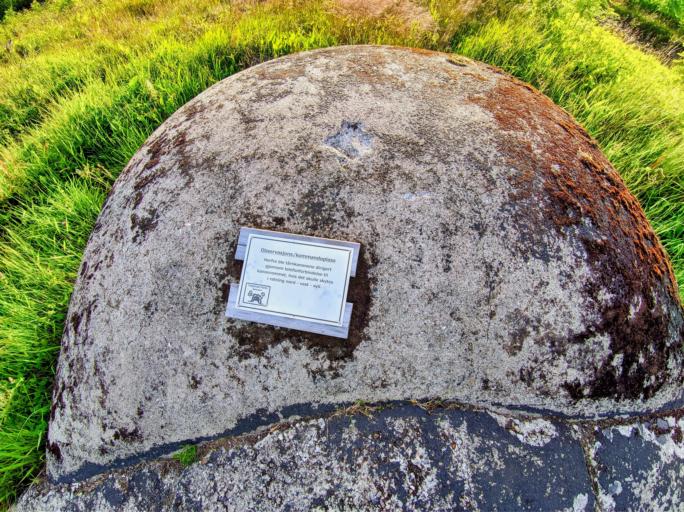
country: NO
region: Ostfold
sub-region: Trogstad
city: Skjonhaug
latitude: 59.6323
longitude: 11.3451
